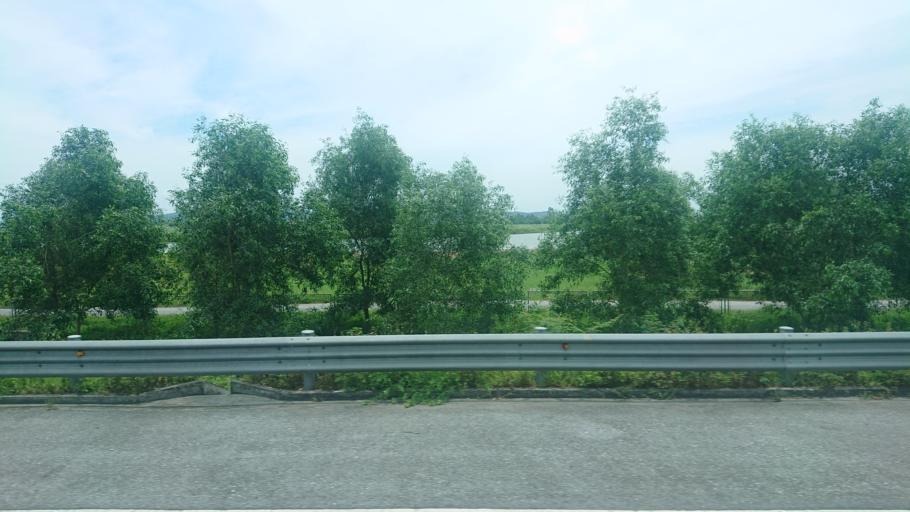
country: VN
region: Hai Phong
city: An Lao
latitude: 20.7796
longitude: 106.5712
